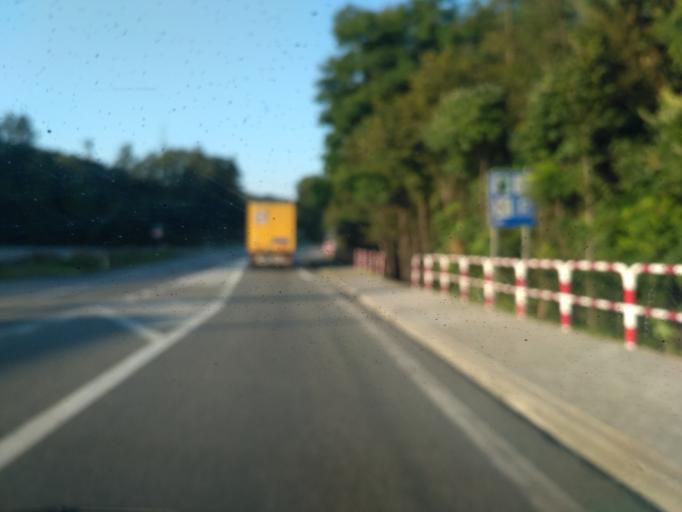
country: PL
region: Subcarpathian Voivodeship
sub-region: Powiat krosnienski
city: Dukla
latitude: 49.5802
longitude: 21.7033
